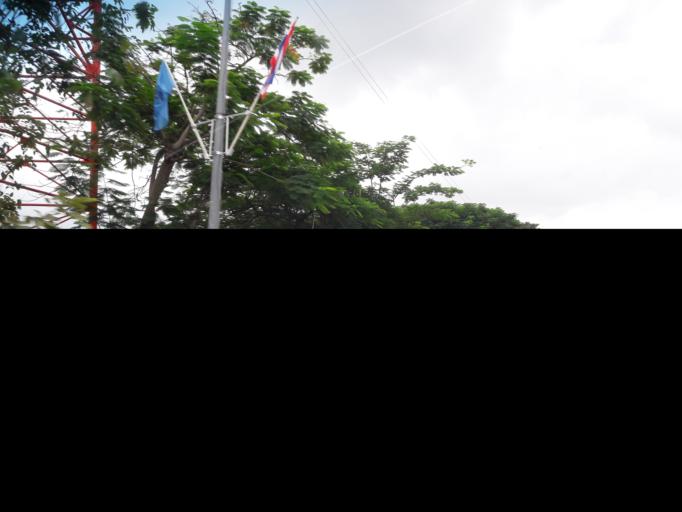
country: TH
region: Ratchaburi
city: Ratchaburi
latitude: 13.5494
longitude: 99.8241
